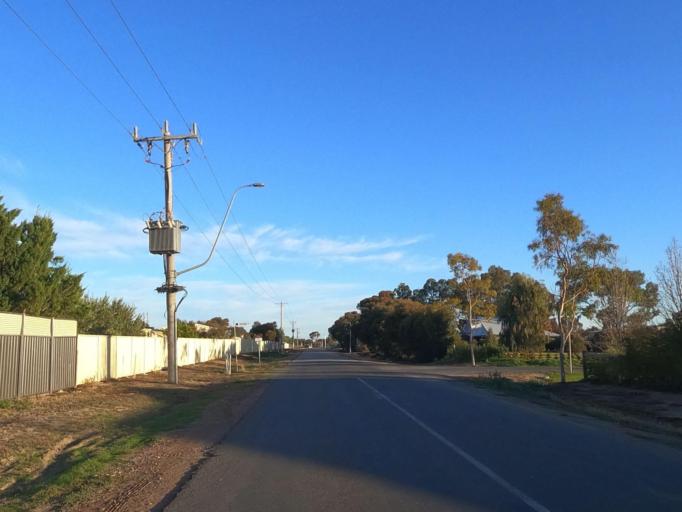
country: AU
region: Victoria
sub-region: Swan Hill
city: Swan Hill
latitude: -35.3297
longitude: 143.5347
